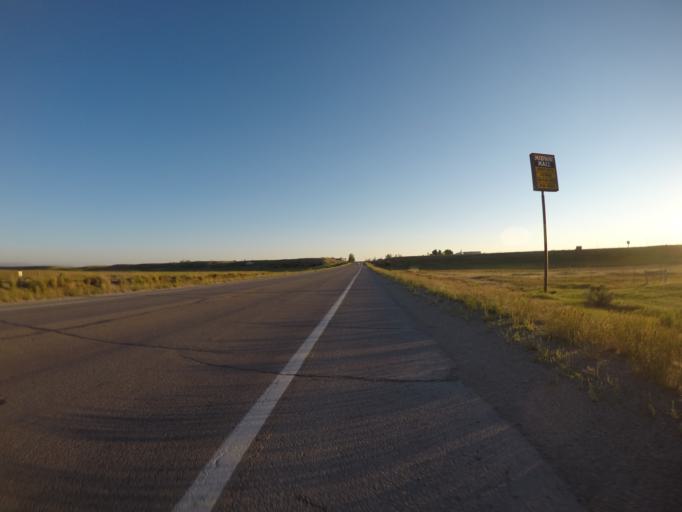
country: US
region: Wyoming
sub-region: Sublette County
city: Marbleton
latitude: 42.5470
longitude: -110.1095
